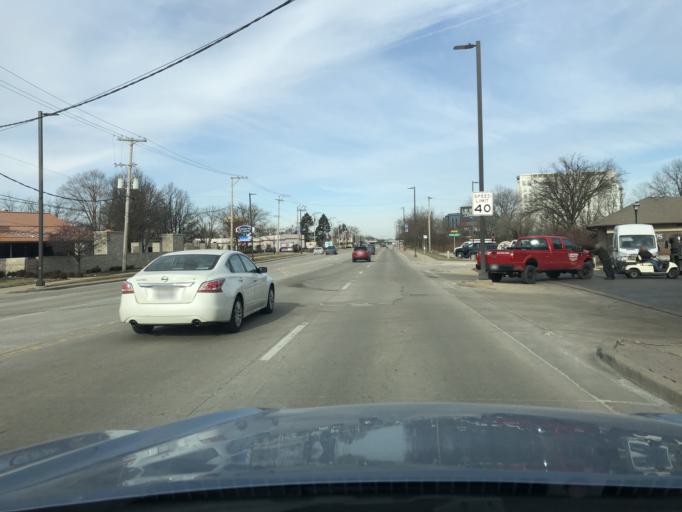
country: US
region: Illinois
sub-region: Cook County
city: Wheeling
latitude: 42.1463
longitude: -87.9109
